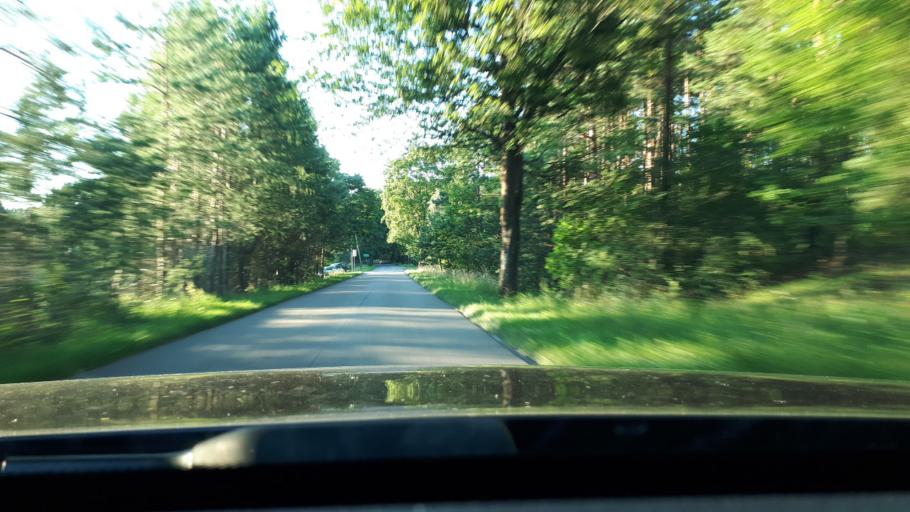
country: PL
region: Warmian-Masurian Voivodeship
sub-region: Powiat olsztynski
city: Stawiguda
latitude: 53.6055
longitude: 20.4233
